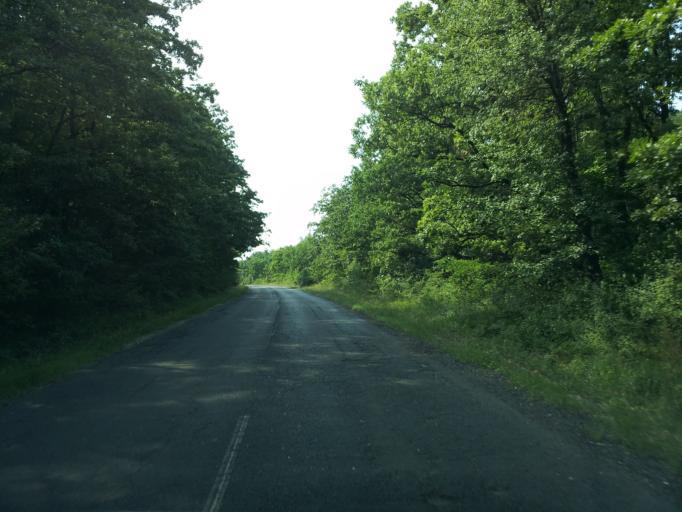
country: HU
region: Veszprem
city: Balatonfured
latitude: 46.9927
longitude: 17.8097
